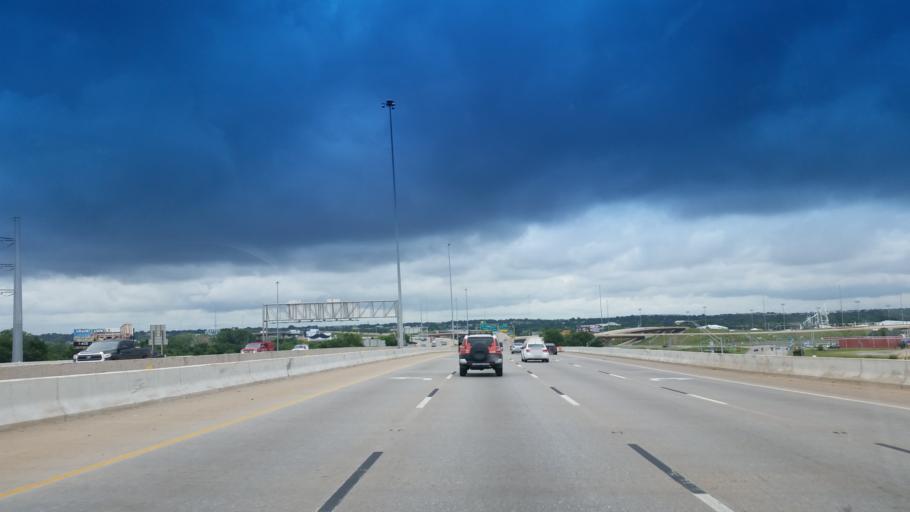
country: US
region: Oklahoma
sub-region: Oklahoma County
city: Oklahoma City
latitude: 35.4690
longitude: -97.5028
